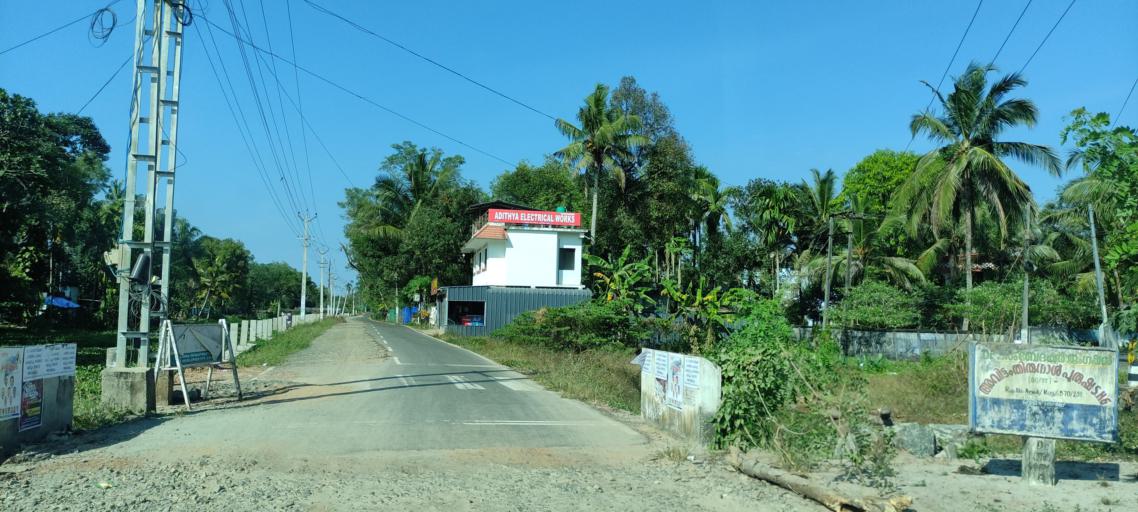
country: IN
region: Kerala
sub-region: Alappuzha
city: Alleppey
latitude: 9.5681
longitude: 76.3304
